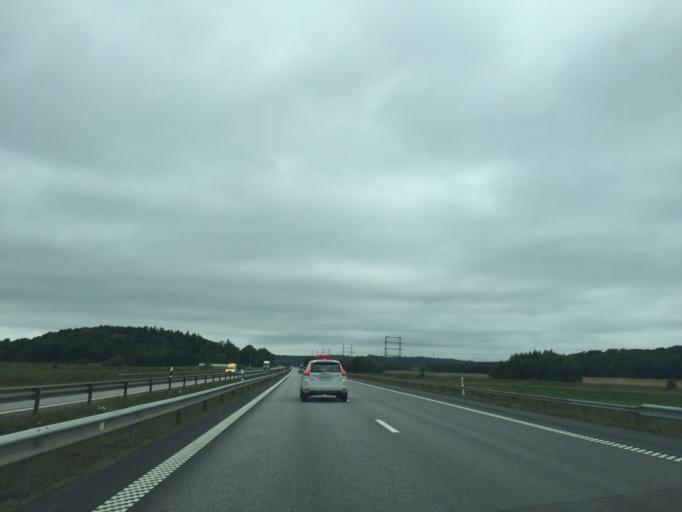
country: SE
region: Halland
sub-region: Kungsbacka Kommun
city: Kungsbacka
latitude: 57.4582
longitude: 12.0848
